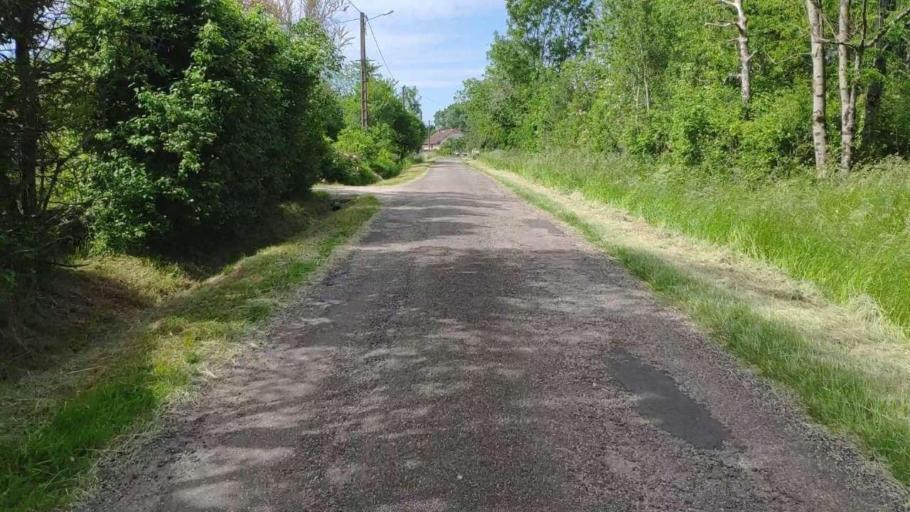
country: FR
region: Franche-Comte
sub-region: Departement du Jura
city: Bletterans
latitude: 46.7099
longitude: 5.4569
